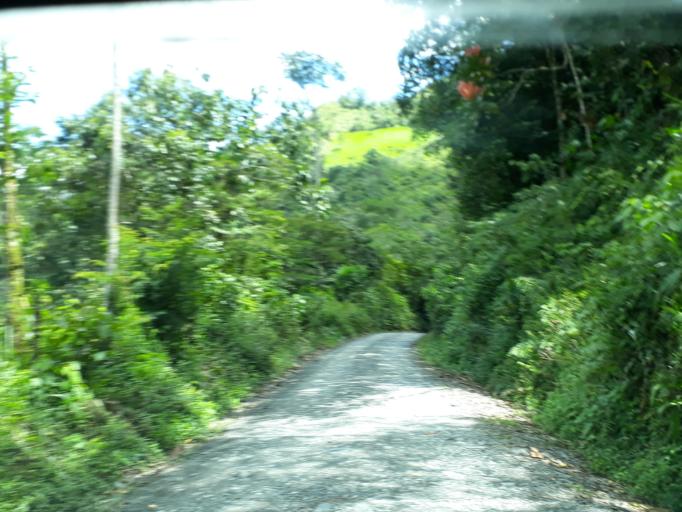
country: CO
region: Cundinamarca
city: Topaipi
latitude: 5.3530
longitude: -74.1981
